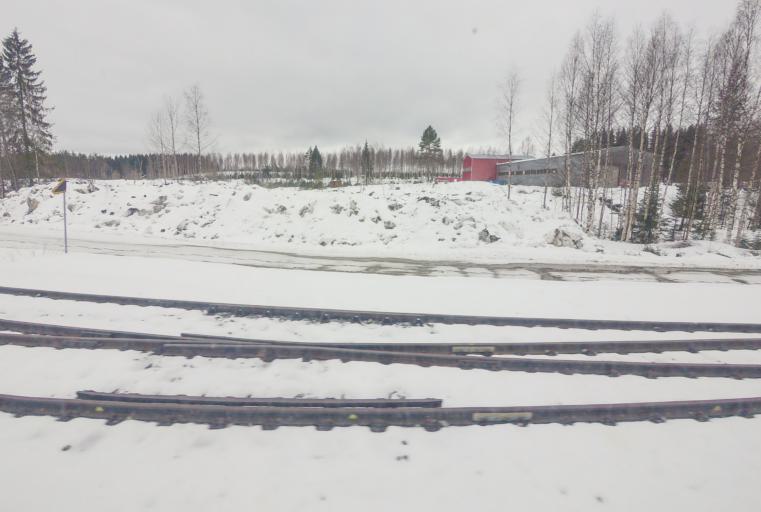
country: FI
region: Southern Savonia
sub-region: Savonlinna
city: Kerimaeki
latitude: 61.8623
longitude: 29.1109
